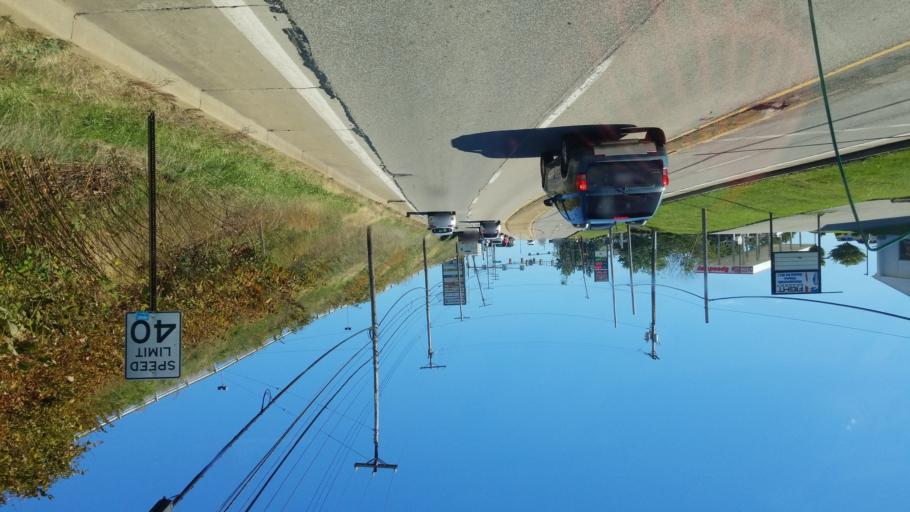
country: US
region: Pennsylvania
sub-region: Allegheny County
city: East McKeesport
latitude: 40.3699
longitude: -79.7844
